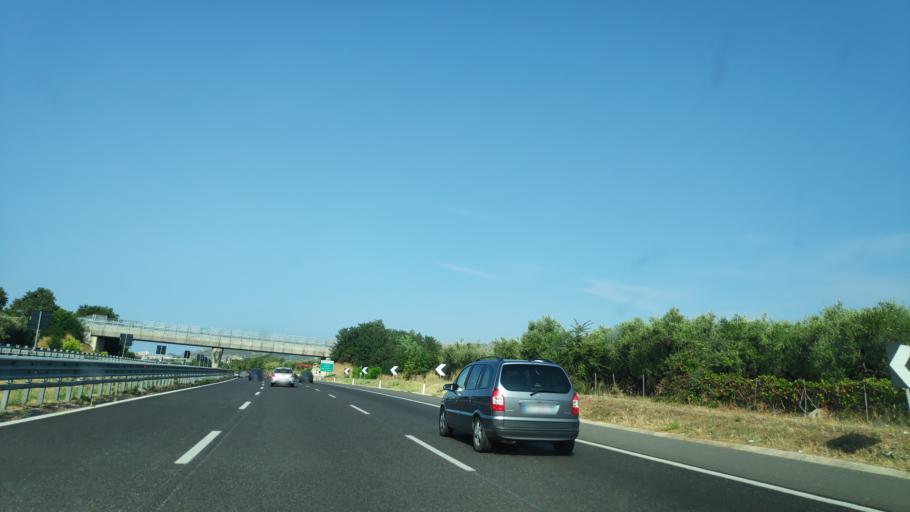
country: IT
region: Campania
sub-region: Provincia di Salerno
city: Eboli
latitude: 40.6098
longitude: 15.0825
